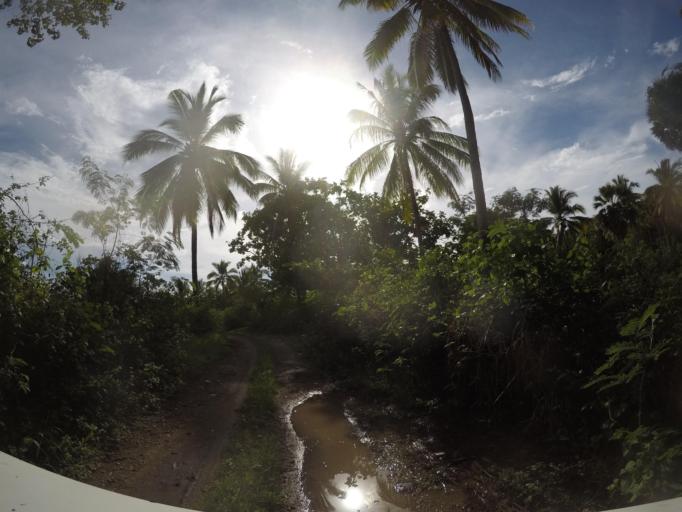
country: TL
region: Baucau
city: Baucau
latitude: -8.5036
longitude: 126.4504
